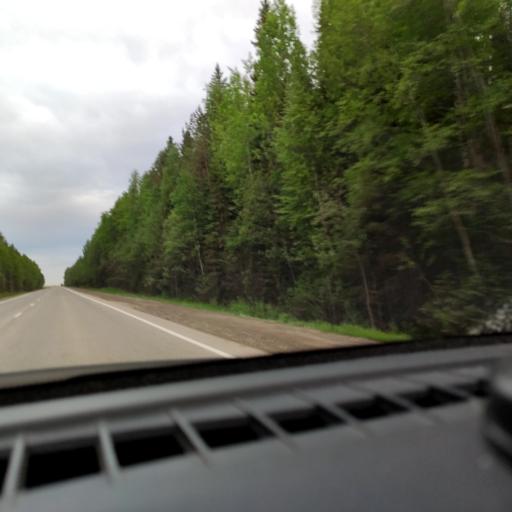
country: RU
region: Perm
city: Ust'-Kachka
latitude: 57.9124
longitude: 55.7711
